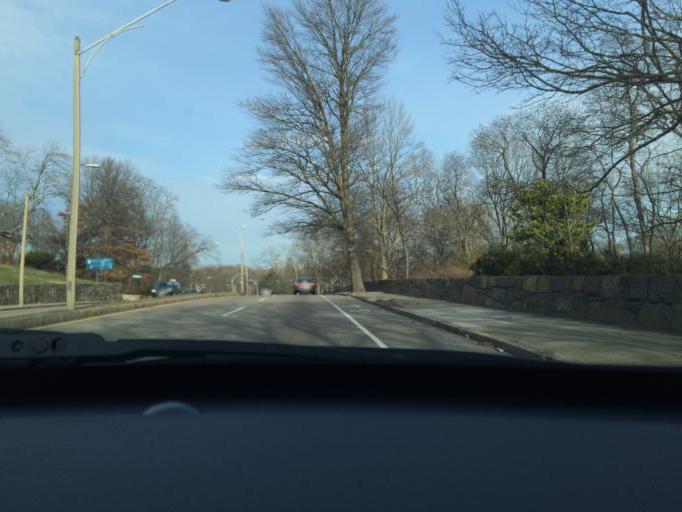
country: US
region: Massachusetts
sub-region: Suffolk County
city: Jamaica Plain
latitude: 42.3013
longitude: -71.1267
